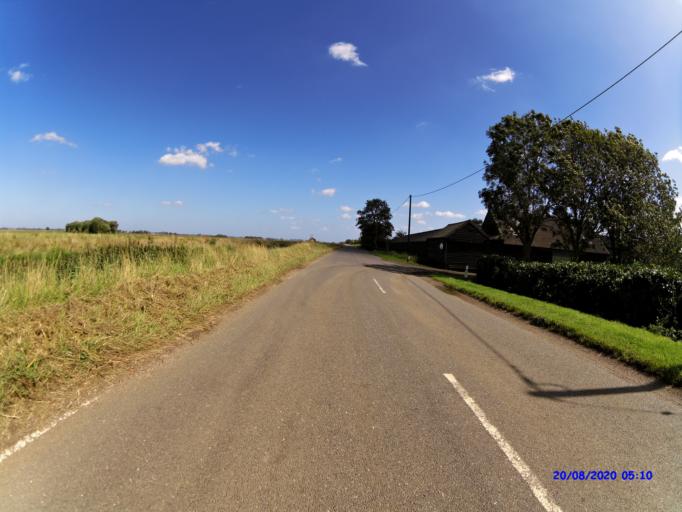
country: GB
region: England
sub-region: Cambridgeshire
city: Whittlesey
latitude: 52.5176
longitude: -0.1284
